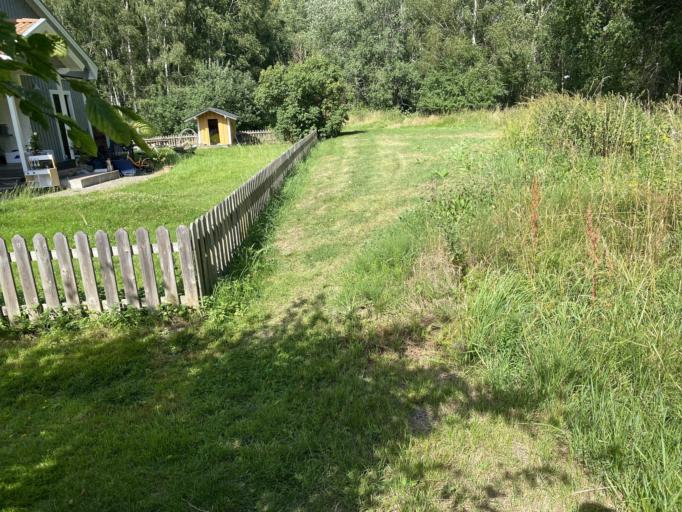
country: SE
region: Stockholm
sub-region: Upplands Vasby Kommun
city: Upplands Vaesby
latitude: 59.4857
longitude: 17.8967
